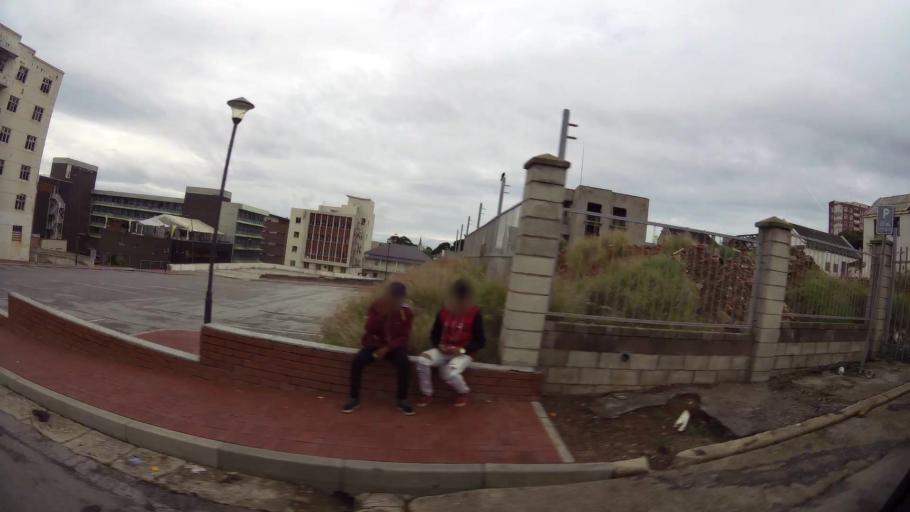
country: ZA
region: Eastern Cape
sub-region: Nelson Mandela Bay Metropolitan Municipality
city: Port Elizabeth
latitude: -33.9597
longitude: 25.6193
